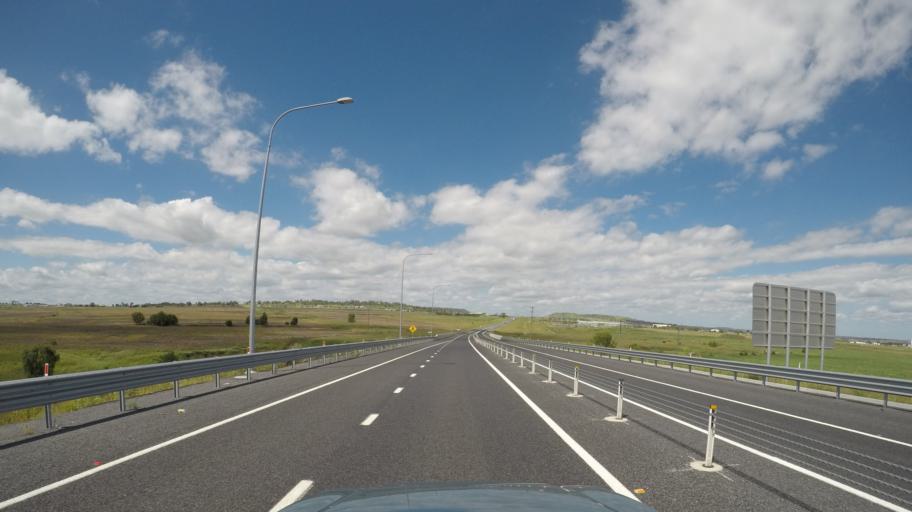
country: AU
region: Queensland
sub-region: Toowoomba
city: Wilsonton Heights
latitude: -27.5309
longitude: 151.8561
